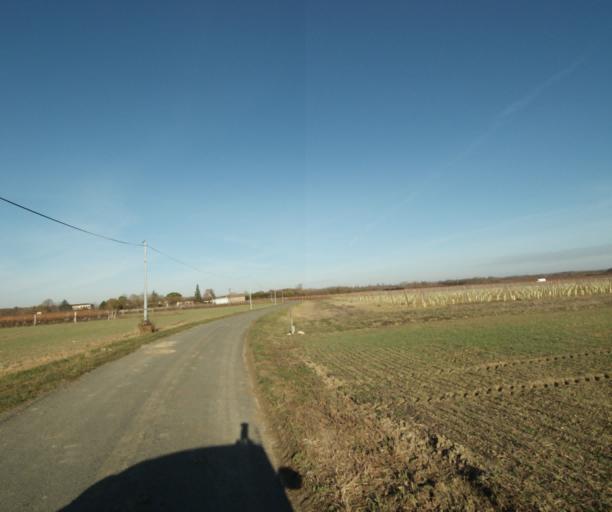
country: FR
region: Poitou-Charentes
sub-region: Departement de la Charente-Maritime
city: Burie
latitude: 45.7920
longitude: -0.4172
